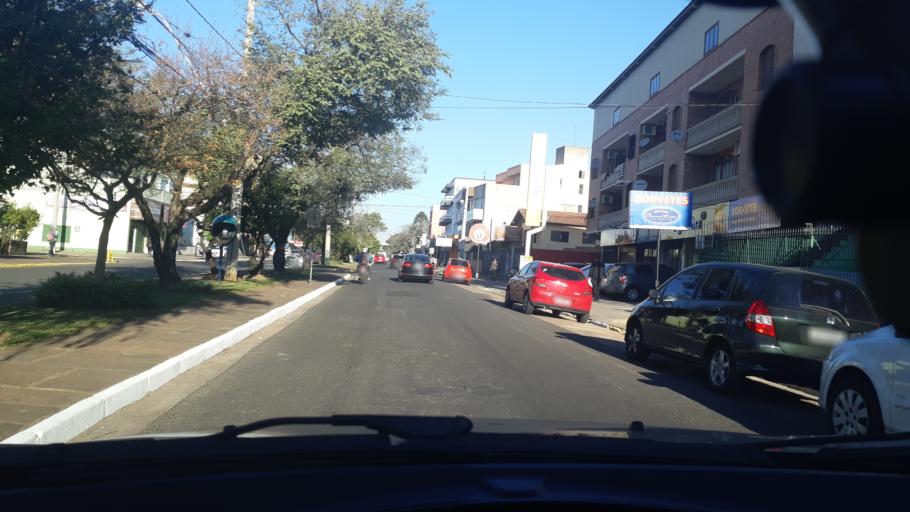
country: BR
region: Rio Grande do Sul
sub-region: Sao Leopoldo
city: Sao Leopoldo
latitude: -29.7725
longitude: -51.1326
